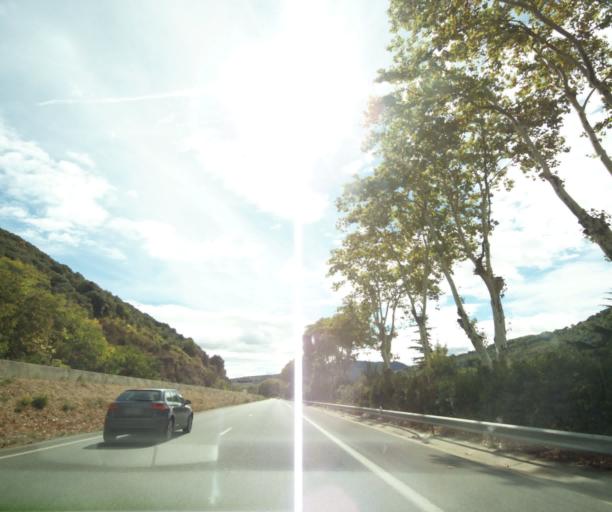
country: FR
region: Languedoc-Roussillon
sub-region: Departement de l'Herault
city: Lodeve
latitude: 43.7161
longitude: 3.3243
